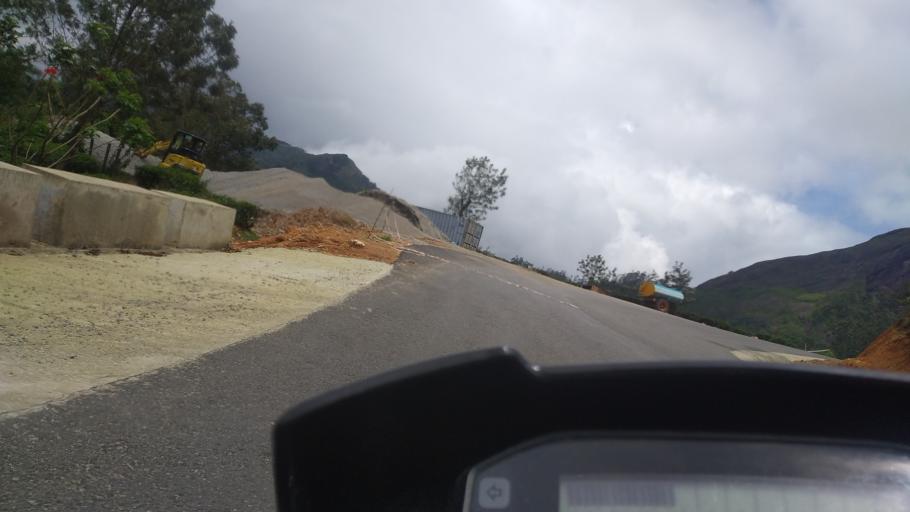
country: IN
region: Kerala
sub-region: Idukki
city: Munnar
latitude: 10.0398
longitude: 77.1126
